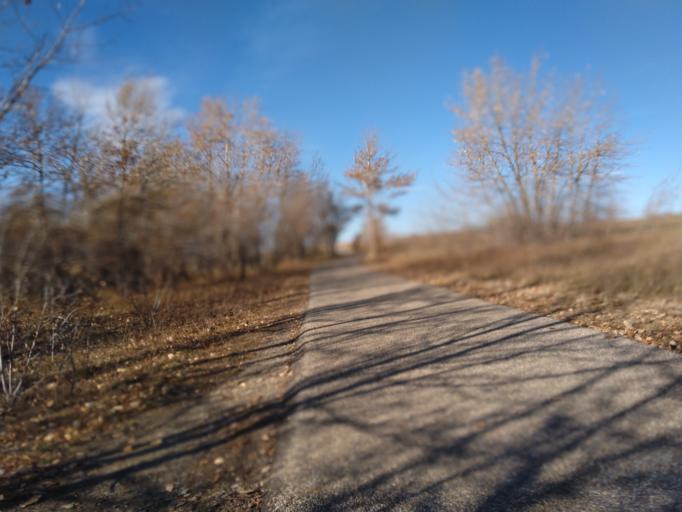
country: CA
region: Alberta
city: Calgary
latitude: 51.1038
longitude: -114.1128
